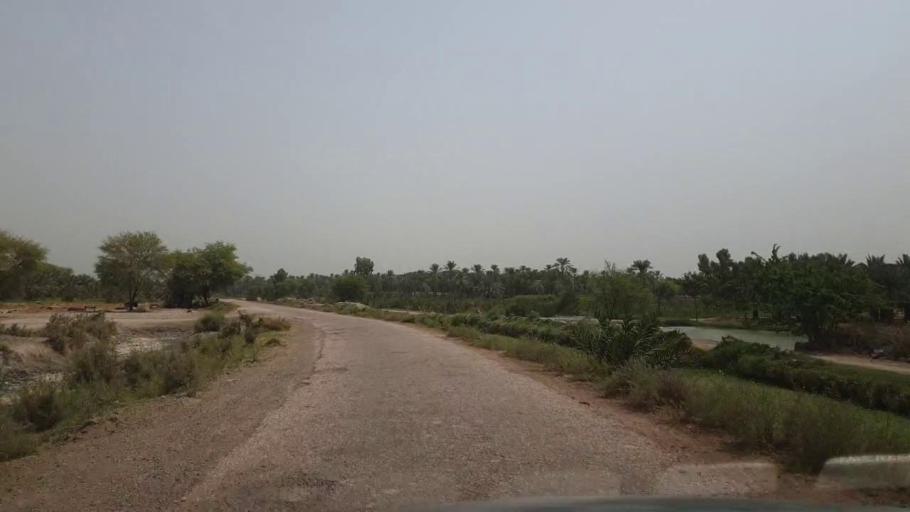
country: PK
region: Sindh
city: Gambat
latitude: 27.4160
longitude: 68.5528
